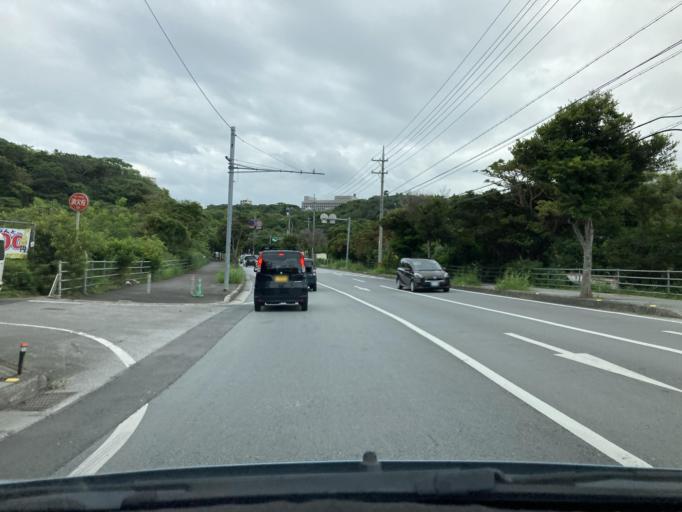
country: JP
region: Okinawa
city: Ginowan
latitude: 26.2481
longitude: 127.7574
